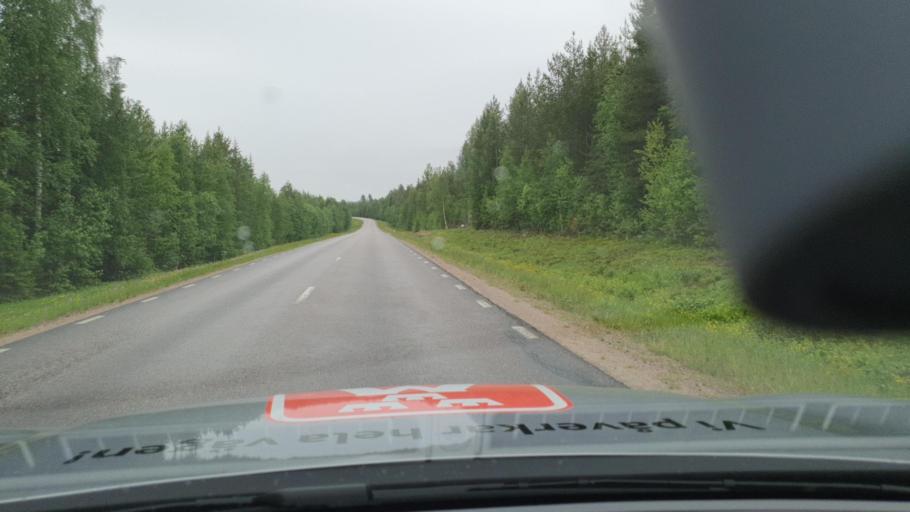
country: SE
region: Norrbotten
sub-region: Overtornea Kommun
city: OEvertornea
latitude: 66.4162
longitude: 23.4164
